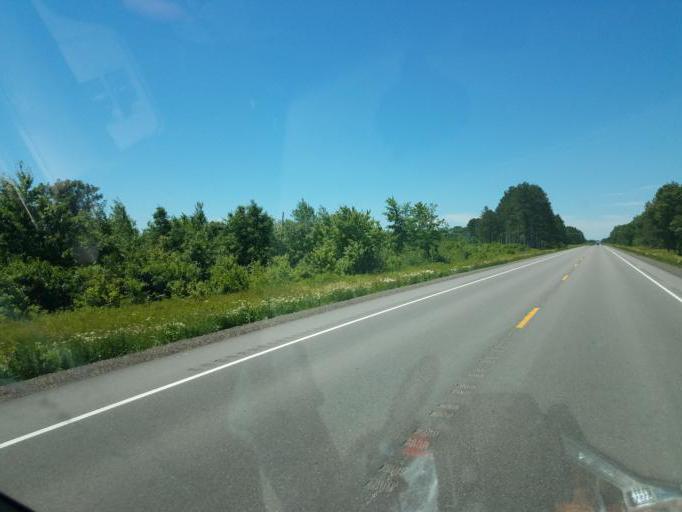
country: US
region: Wisconsin
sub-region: Juneau County
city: New Lisbon
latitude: 44.0246
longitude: -90.1080
